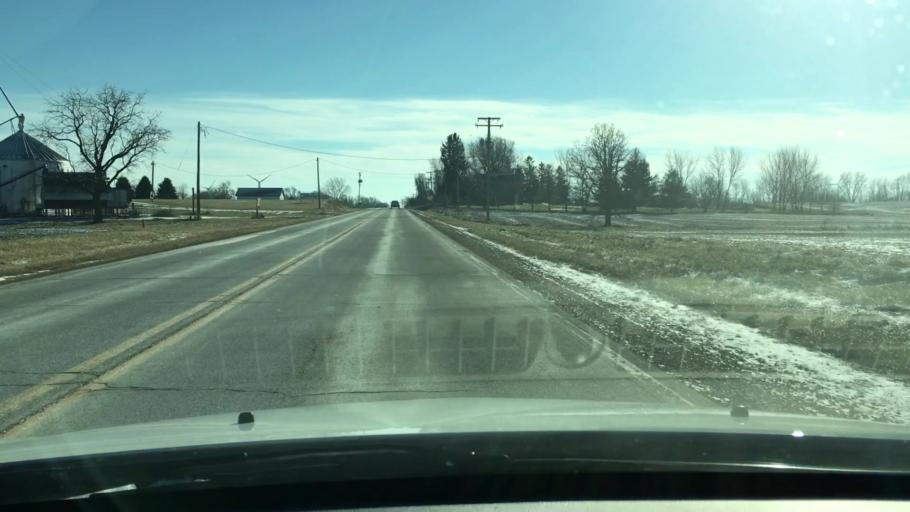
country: US
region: Illinois
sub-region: LaSalle County
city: Mendota
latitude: 41.7005
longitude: -89.0914
